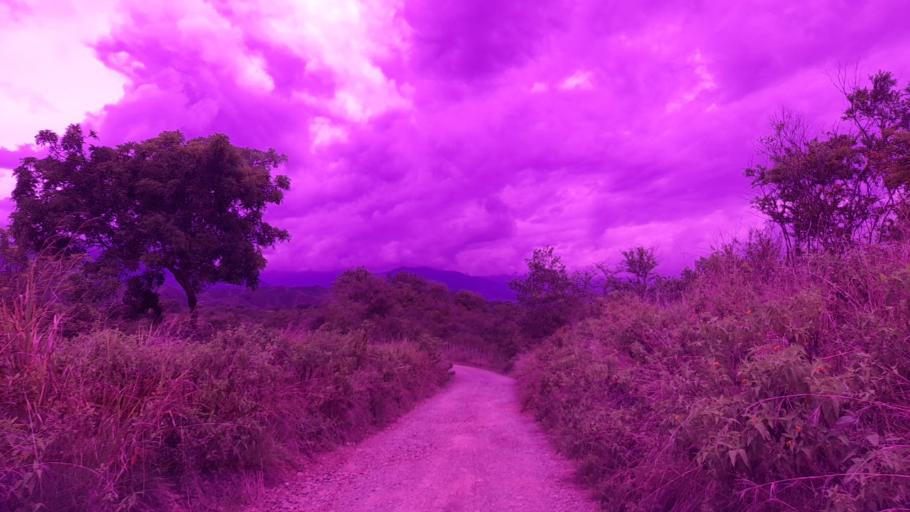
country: CO
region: Valle del Cauca
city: Bugalagrande
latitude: 4.1909
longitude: -76.1414
